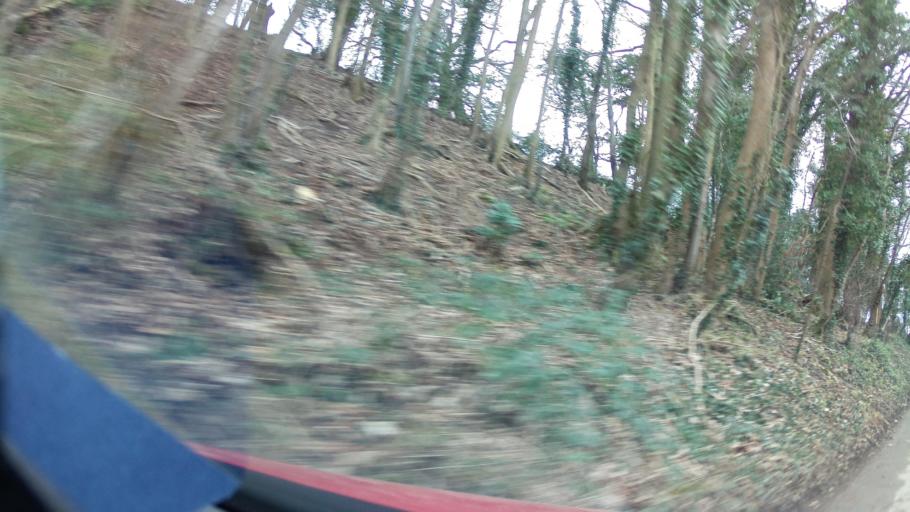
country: GB
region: England
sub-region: Wiltshire
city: Biddestone
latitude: 51.4686
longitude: -2.2338
